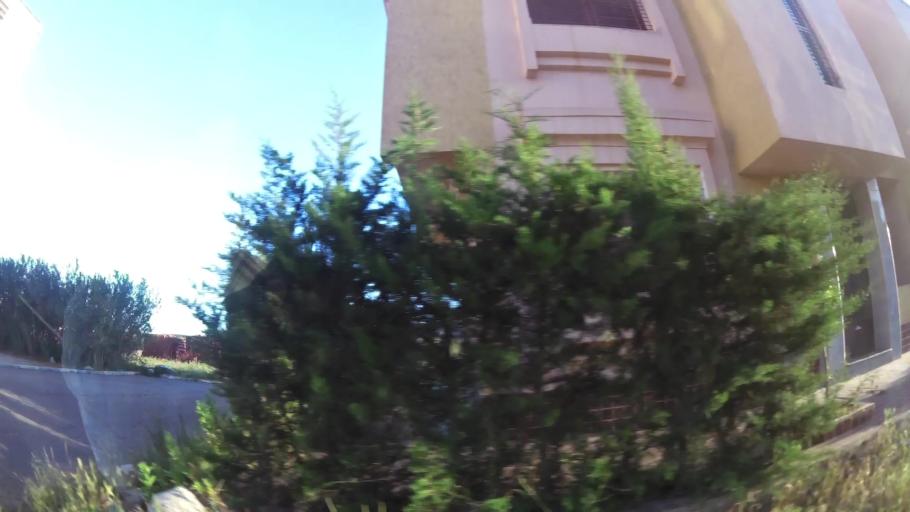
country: MA
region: Oriental
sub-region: Berkane-Taourirt
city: Madagh
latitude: 35.0767
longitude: -2.2337
